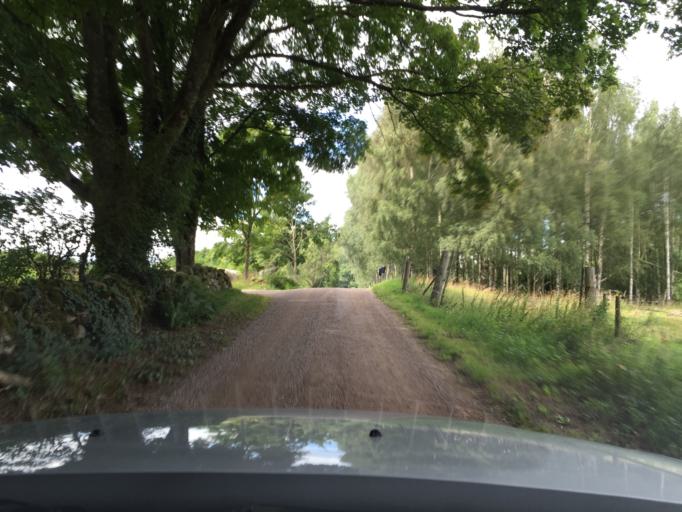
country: SE
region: Skane
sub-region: Hassleholms Kommun
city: Sosdala
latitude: 56.0248
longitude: 13.6448
